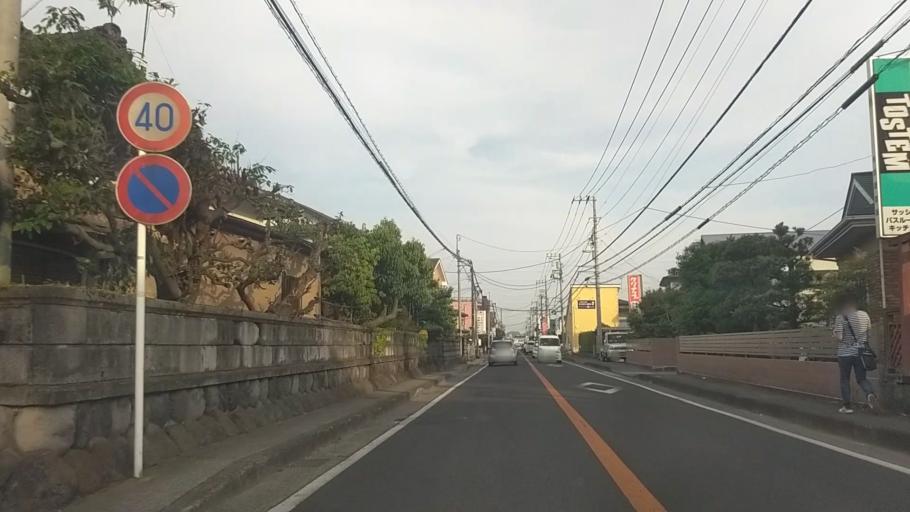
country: JP
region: Kanagawa
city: Odawara
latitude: 35.2982
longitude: 139.1288
